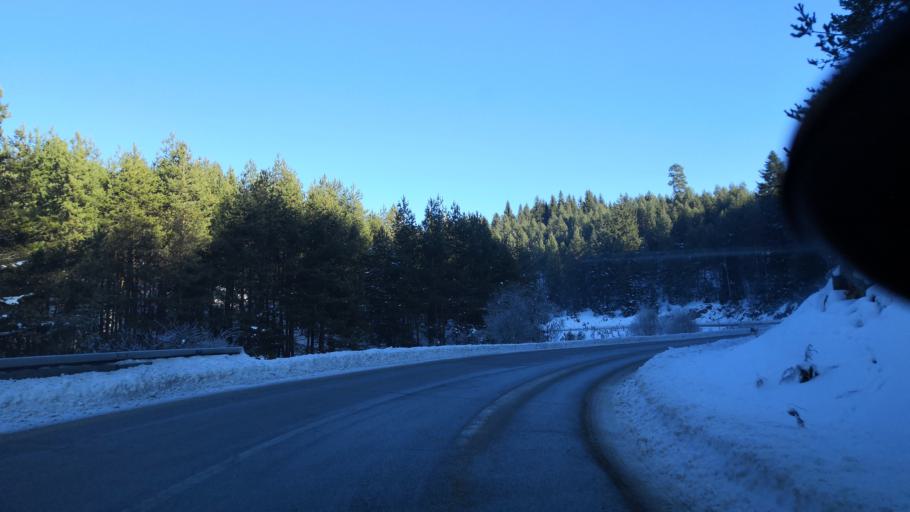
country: BA
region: Republika Srpska
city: Sokolac
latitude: 43.9880
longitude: 18.8684
